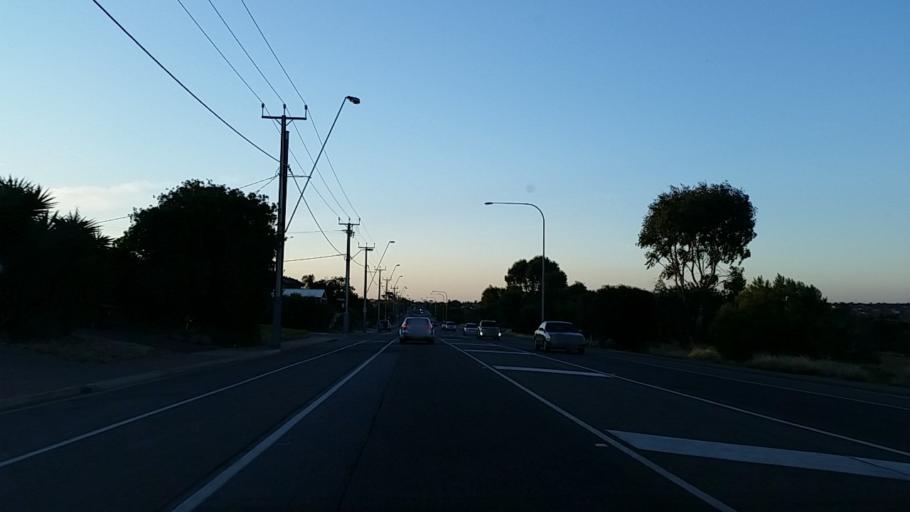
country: AU
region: South Australia
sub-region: Adelaide
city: Port Noarlunga
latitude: -35.1640
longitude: 138.4754
